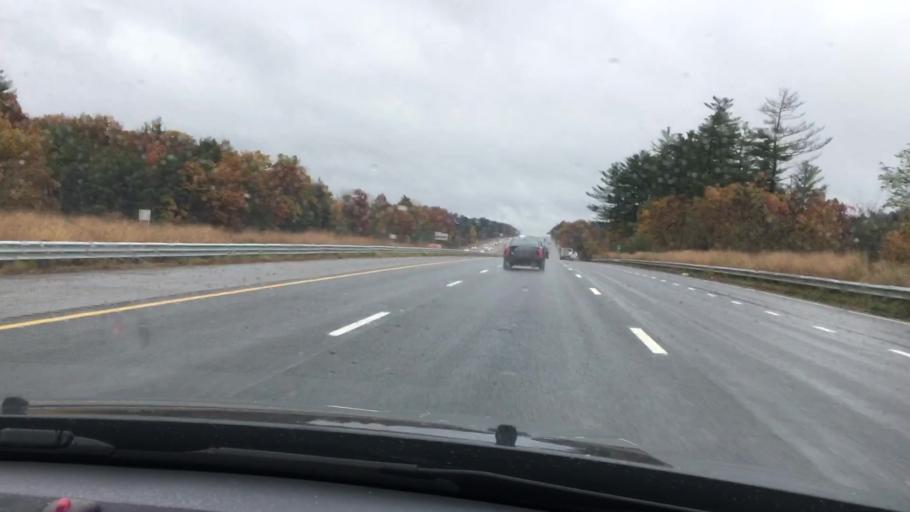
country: US
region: Massachusetts
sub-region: Middlesex County
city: Tyngsboro
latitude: 42.6583
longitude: -71.4282
